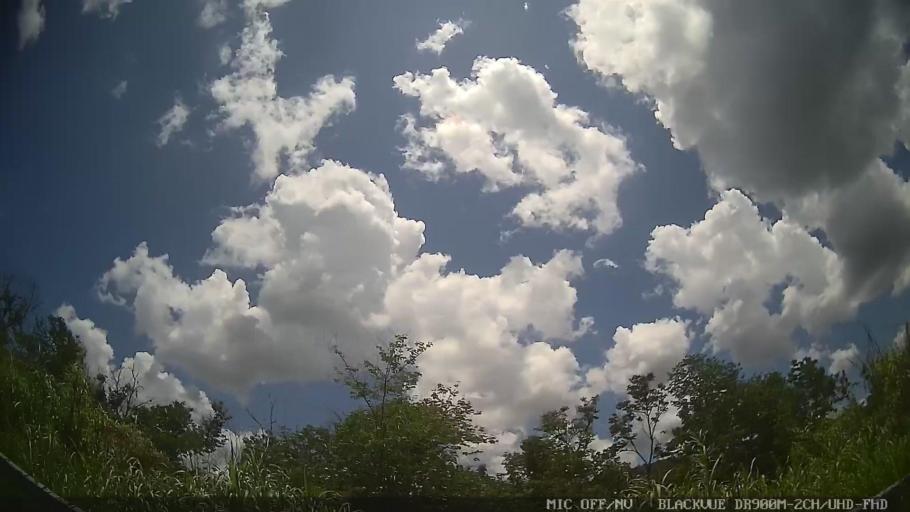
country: BR
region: Sao Paulo
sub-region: Amparo
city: Amparo
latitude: -22.6734
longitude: -46.7396
